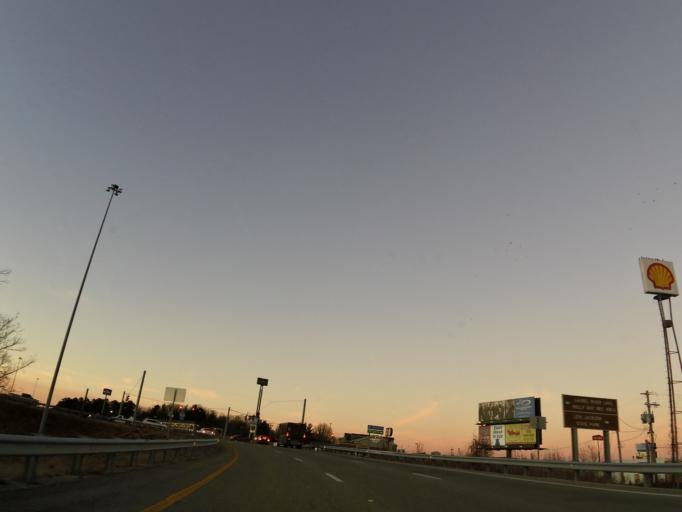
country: US
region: Kentucky
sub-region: Laurel County
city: London
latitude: 37.1100
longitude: -84.1006
